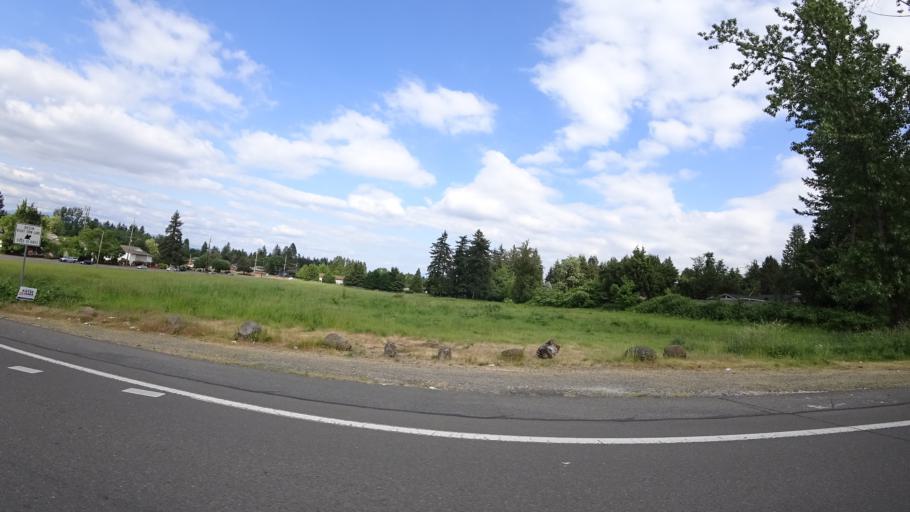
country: US
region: Oregon
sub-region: Multnomah County
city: Fairview
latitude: 45.5333
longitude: -122.4959
